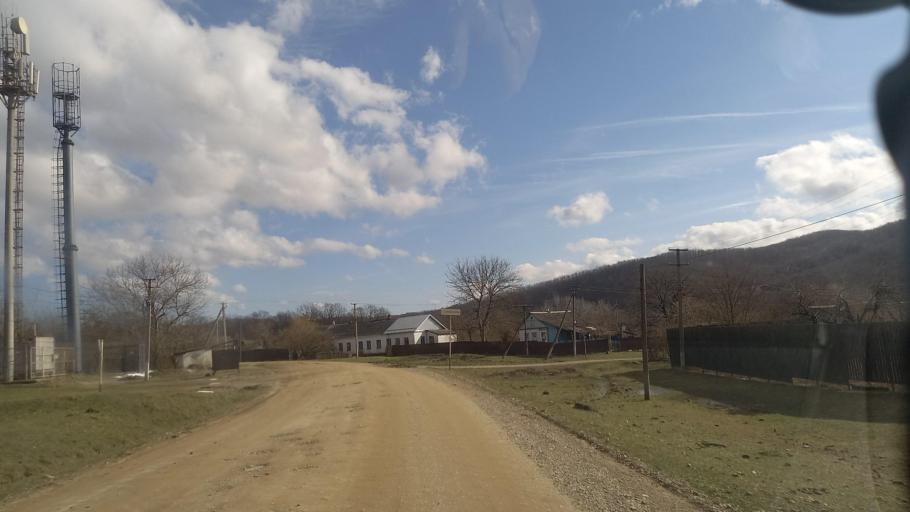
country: RU
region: Krasnodarskiy
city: Smolenskaya
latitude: 44.6031
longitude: 38.8581
